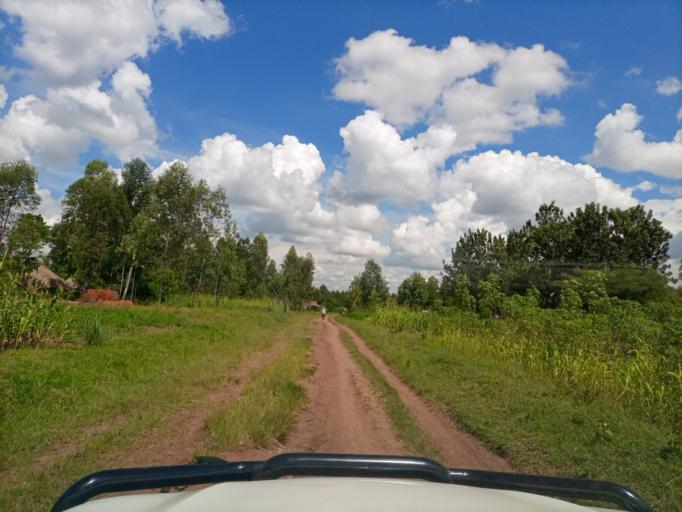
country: UG
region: Eastern Region
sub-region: Tororo District
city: Tororo
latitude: 0.7229
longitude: 34.0199
